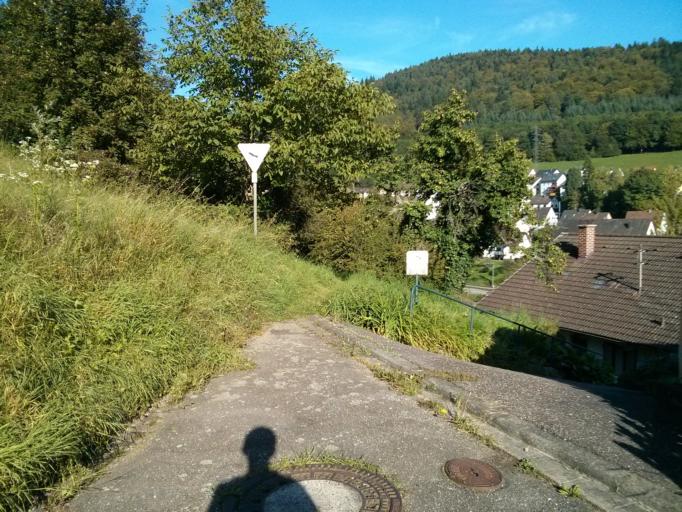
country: DE
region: Baden-Wuerttemberg
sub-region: Karlsruhe Region
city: Gernsbach
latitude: 48.7476
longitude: 8.3456
